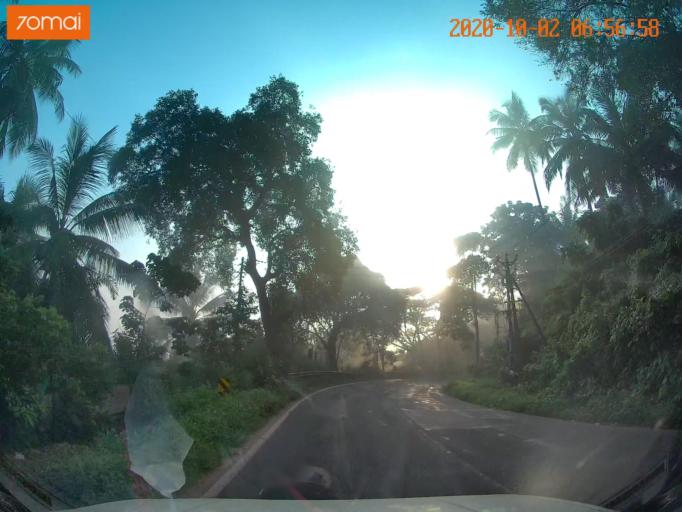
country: IN
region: Kerala
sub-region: Malappuram
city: Tirur
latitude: 10.8681
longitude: 76.0509
